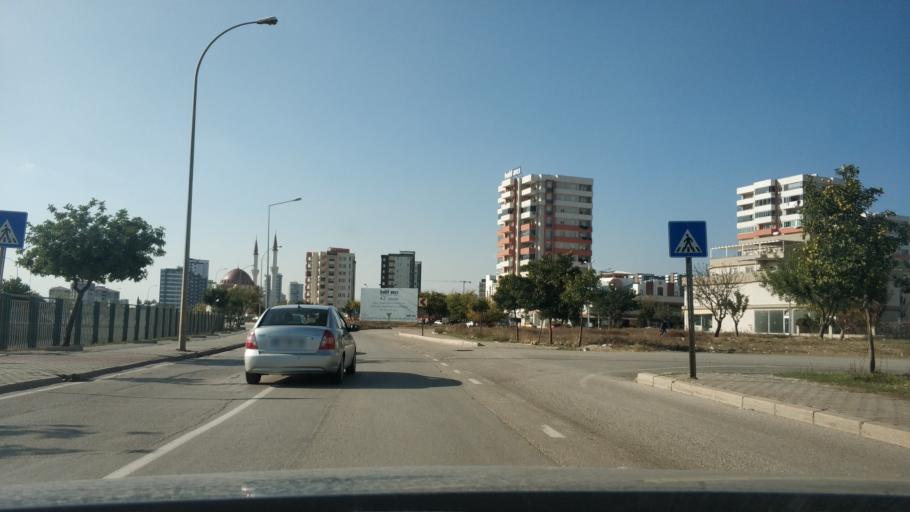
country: TR
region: Adana
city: Seyhan
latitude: 37.0099
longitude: 35.2659
